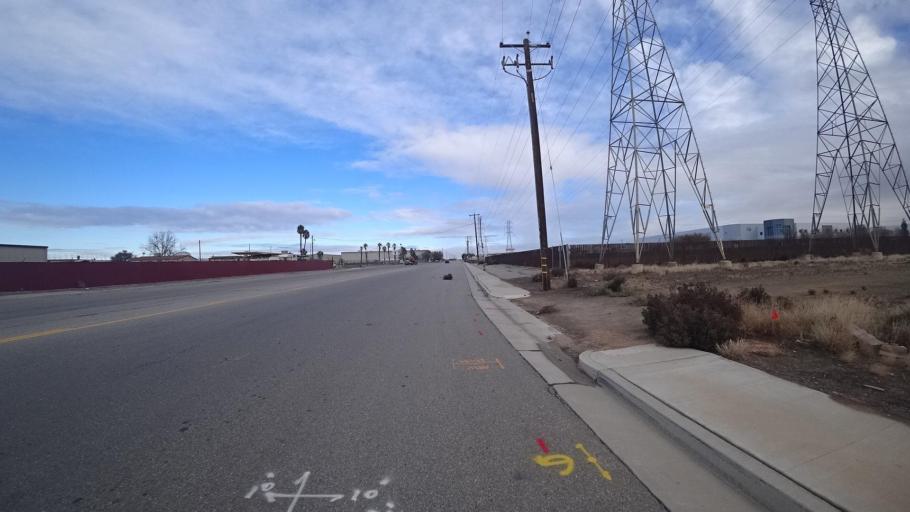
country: US
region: California
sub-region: Kern County
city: Greenacres
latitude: 35.4438
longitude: -119.0828
